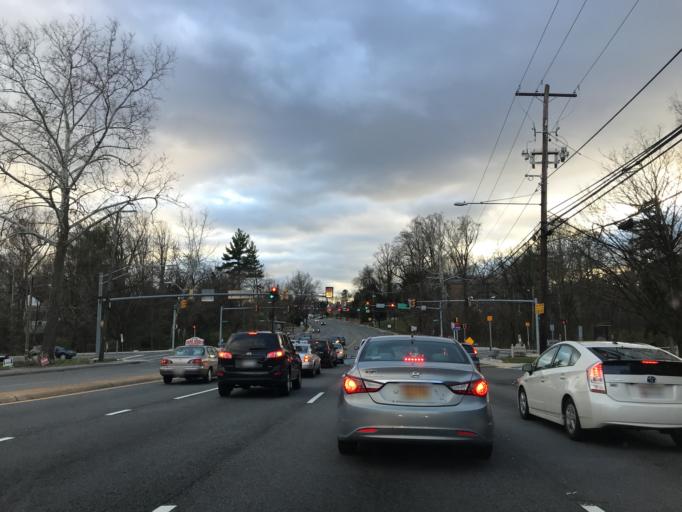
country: US
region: Maryland
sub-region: Montgomery County
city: Four Corners
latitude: 39.0083
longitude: -77.0194
